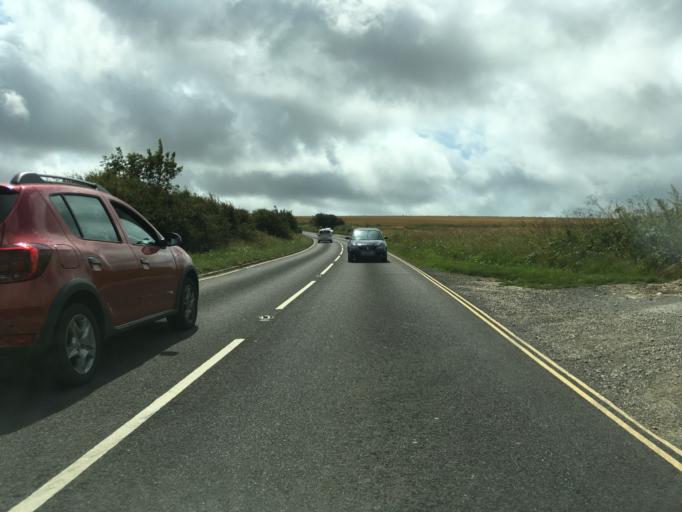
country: GB
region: England
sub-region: Brighton and Hove
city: Rottingdean
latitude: 50.8555
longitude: -0.0770
